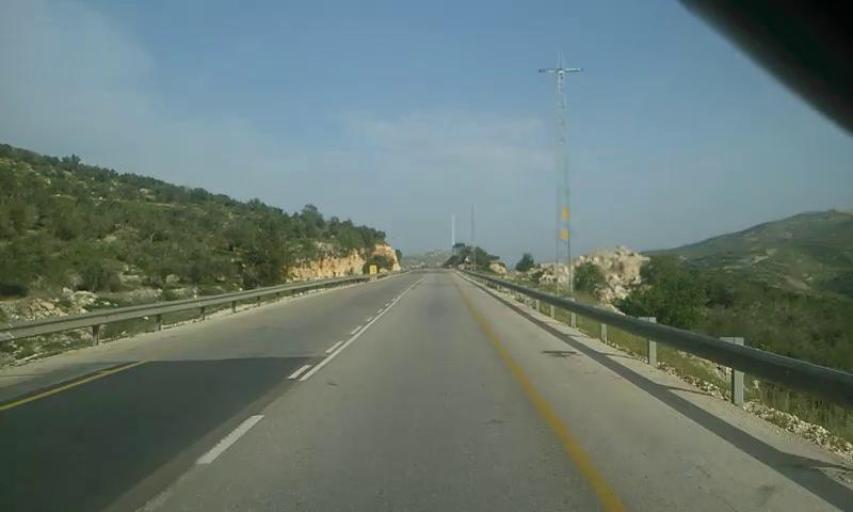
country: PS
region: West Bank
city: `Asirah al Qibliyah
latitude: 32.1879
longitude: 35.2177
